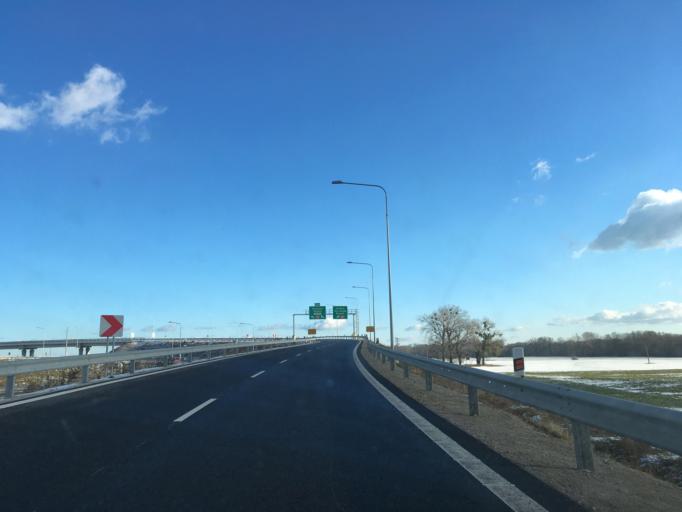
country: SK
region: Bratislavsky
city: Dunajska Luzna
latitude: 48.0897
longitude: 17.1835
